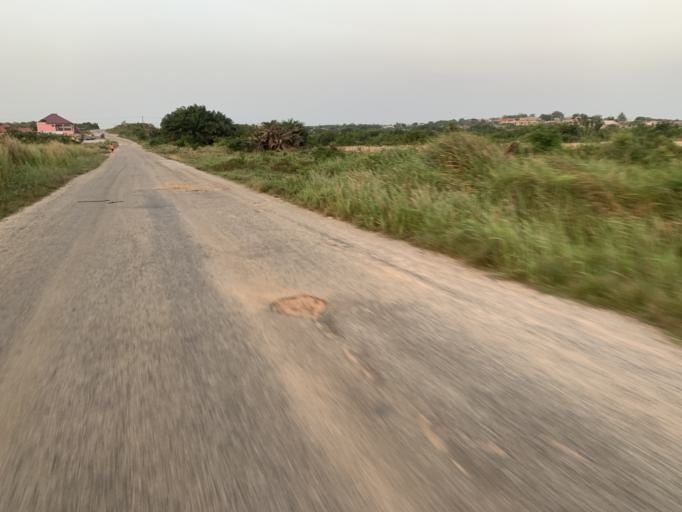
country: GH
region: Central
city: Winneba
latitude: 5.3749
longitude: -0.6130
